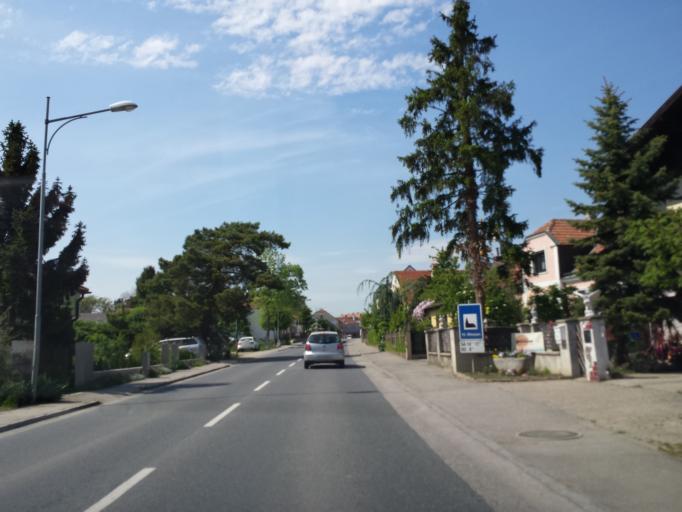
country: AT
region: Lower Austria
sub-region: Politischer Bezirk Tulln
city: Atzenbrugg
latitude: 48.2977
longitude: 15.8966
